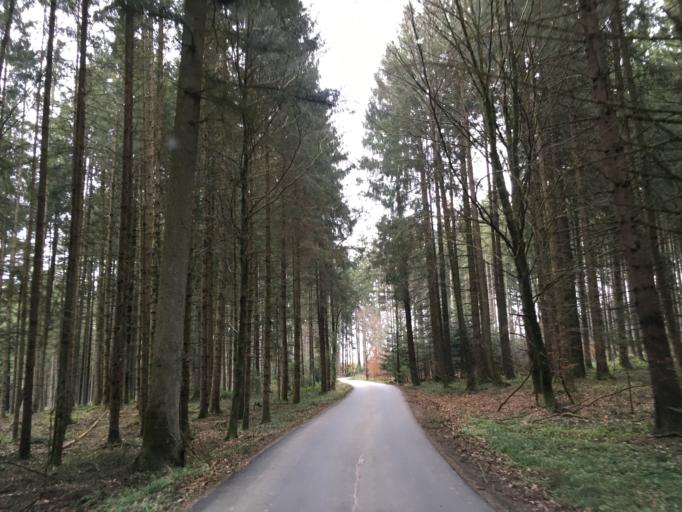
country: DE
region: Bavaria
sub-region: Upper Bavaria
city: Schnaitsee
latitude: 48.0602
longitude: 12.3771
